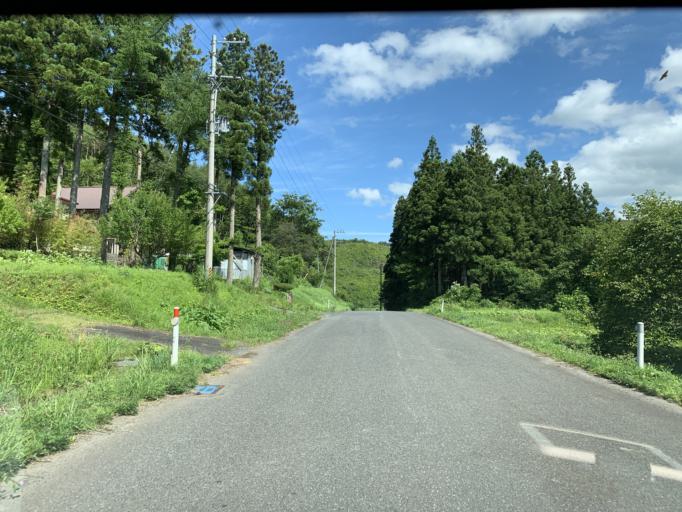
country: JP
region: Iwate
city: Ichinoseki
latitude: 38.9626
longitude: 140.9568
